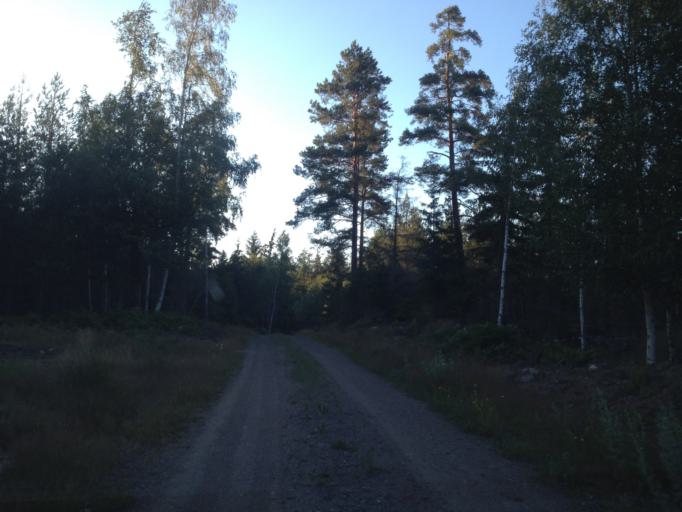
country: SE
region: Kalmar
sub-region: Vasterviks Kommun
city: Overum
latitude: 57.9953
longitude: 16.1689
